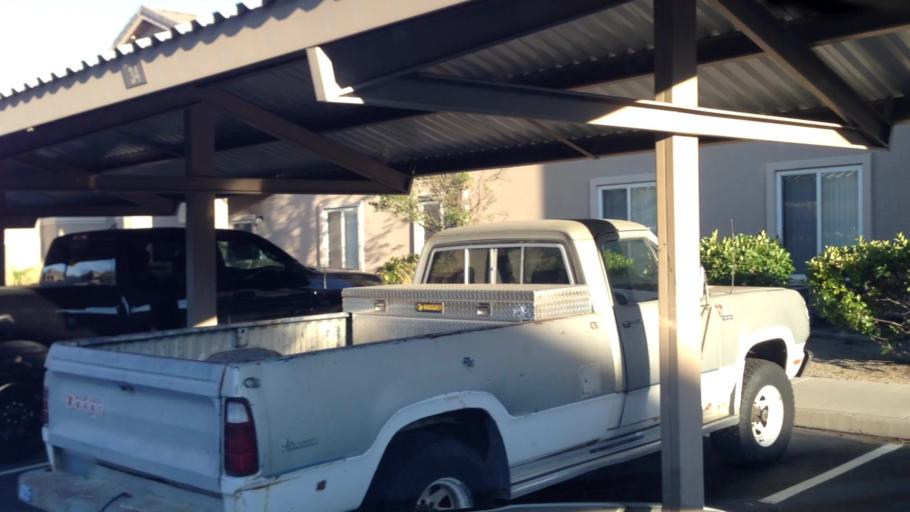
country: US
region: Nevada
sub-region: Washoe County
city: Sparks
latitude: 39.4508
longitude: -119.7570
